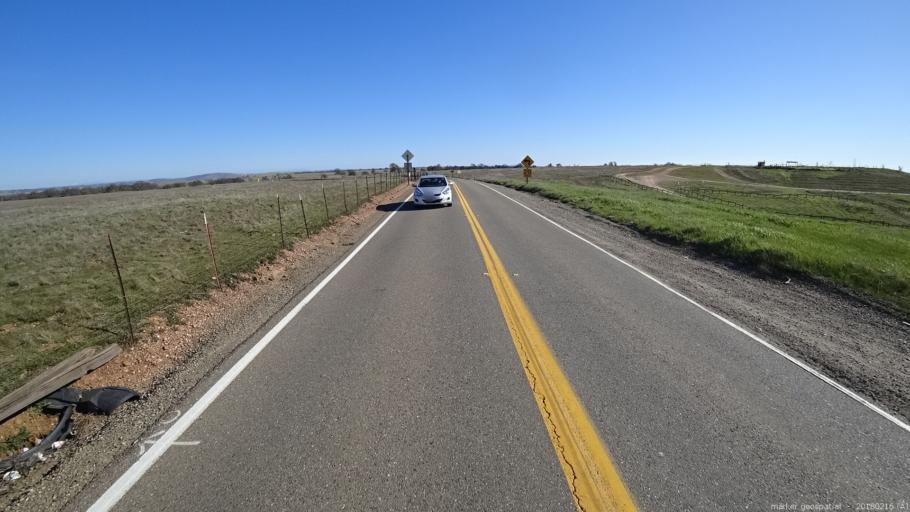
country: US
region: California
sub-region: Sacramento County
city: Folsom
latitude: 38.6058
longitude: -121.1414
